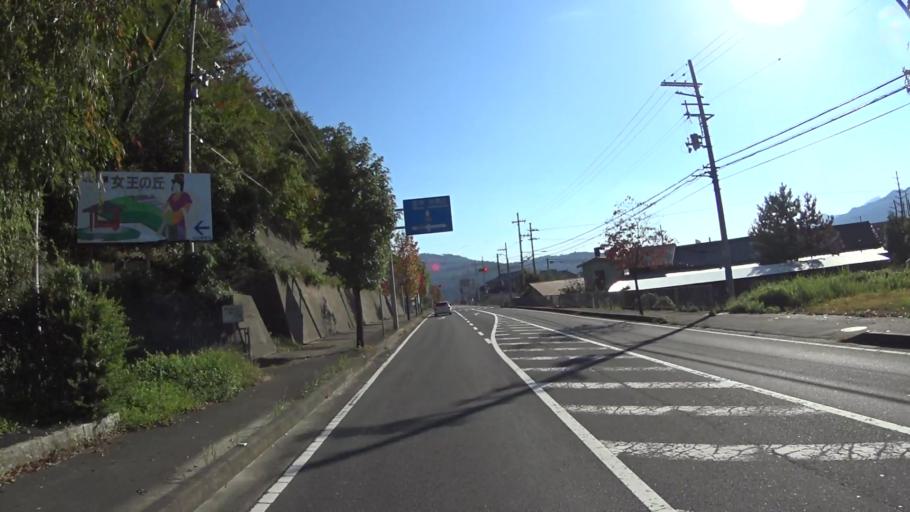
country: JP
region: Kyoto
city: Miyazu
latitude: 35.5797
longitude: 135.0996
